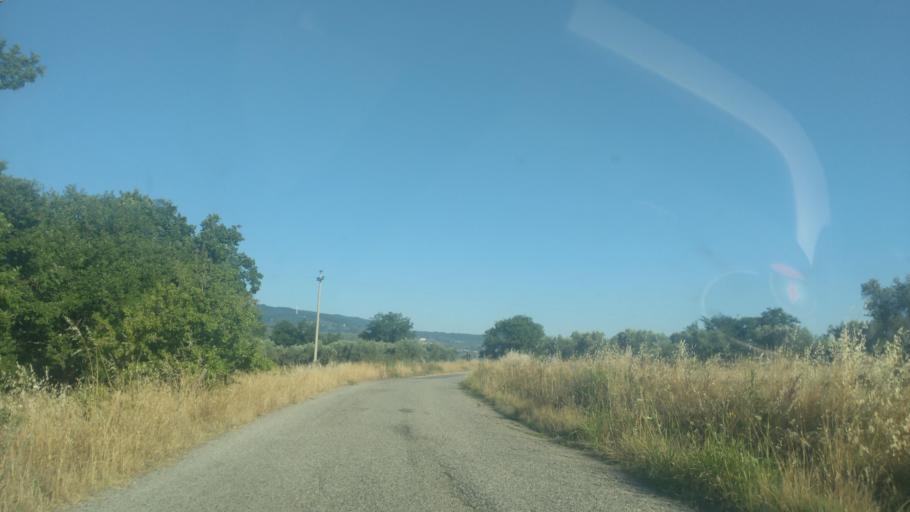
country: IT
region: Calabria
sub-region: Provincia di Catanzaro
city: Squillace
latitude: 38.7748
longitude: 16.4973
